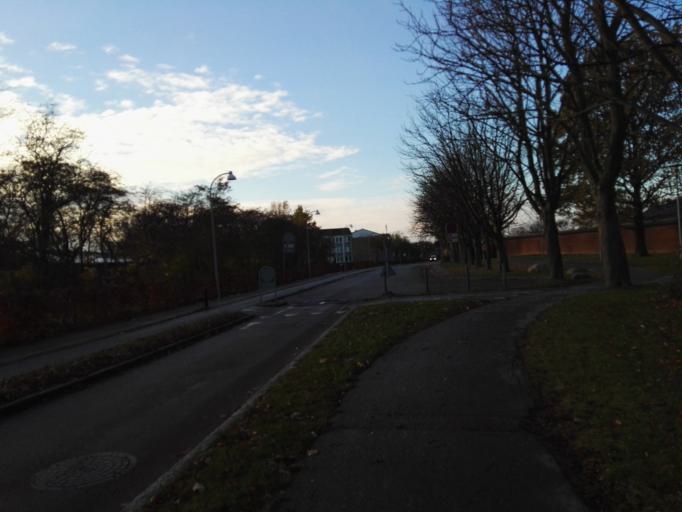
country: DK
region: Capital Region
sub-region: Herlev Kommune
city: Herlev
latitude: 55.7210
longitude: 12.4131
